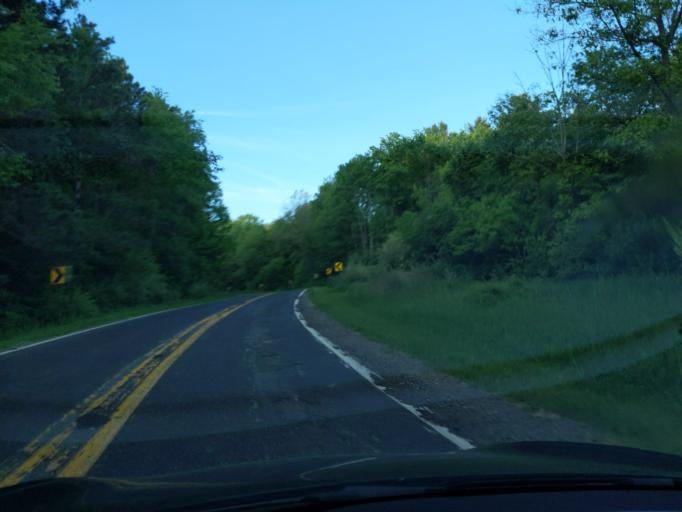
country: US
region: Michigan
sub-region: Ingham County
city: Leslie
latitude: 42.5025
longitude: -84.3134
